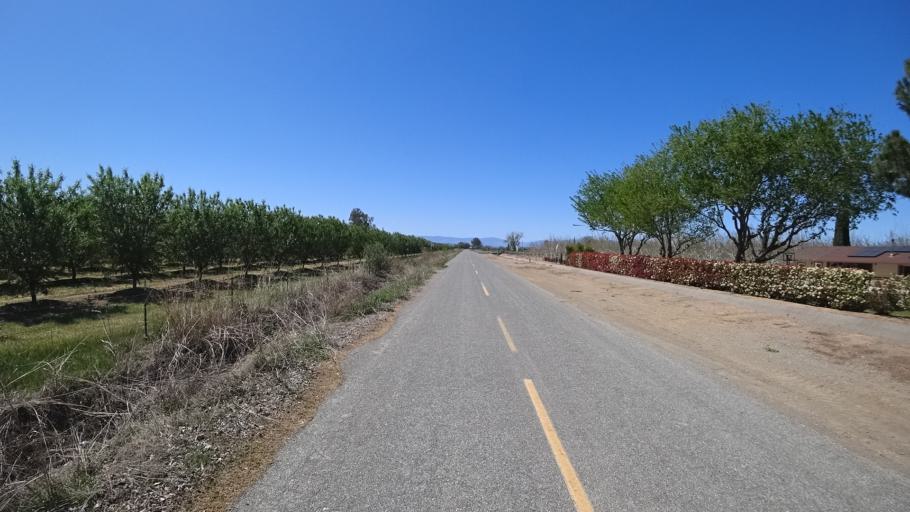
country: US
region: California
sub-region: Glenn County
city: Orland
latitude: 39.7947
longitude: -122.2121
